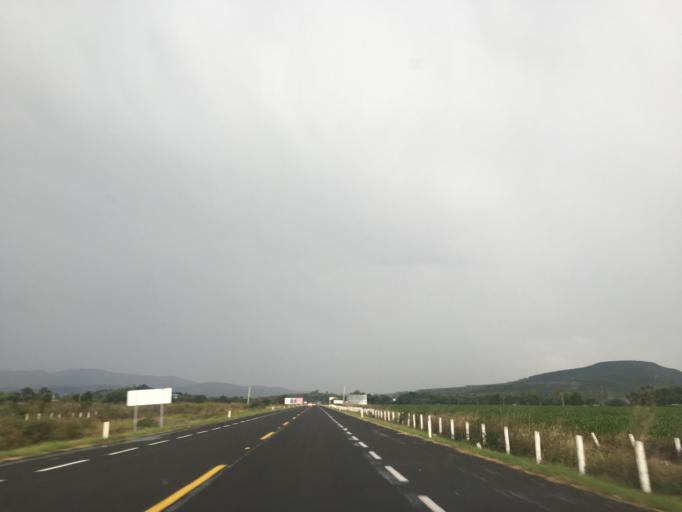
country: MX
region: Michoacan
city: Alvaro Obregon
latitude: 19.8320
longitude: -101.0108
